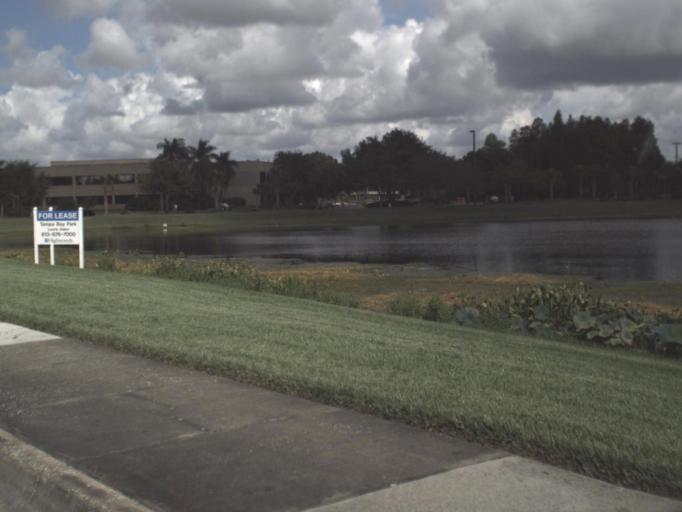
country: US
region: Florida
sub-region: Hillsborough County
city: Egypt Lake-Leto
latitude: 27.9814
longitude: -82.4970
